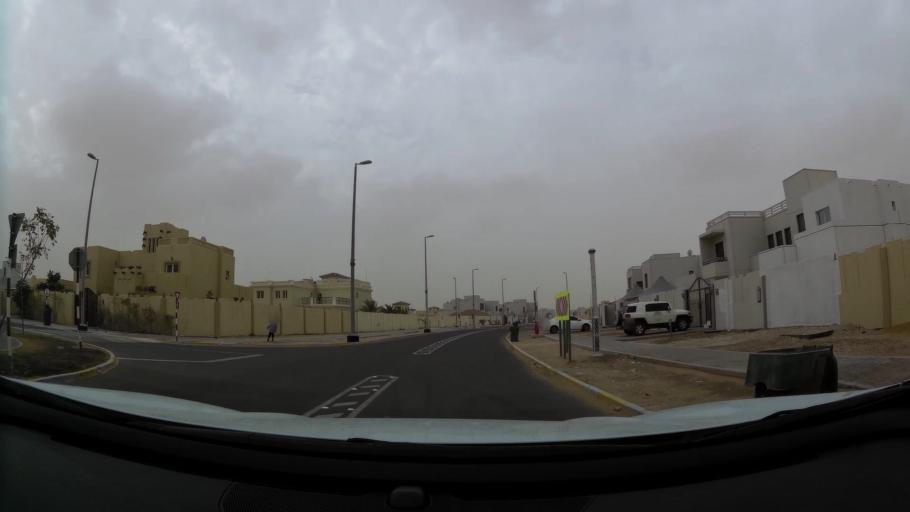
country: AE
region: Abu Dhabi
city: Abu Dhabi
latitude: 24.4355
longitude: 54.7346
